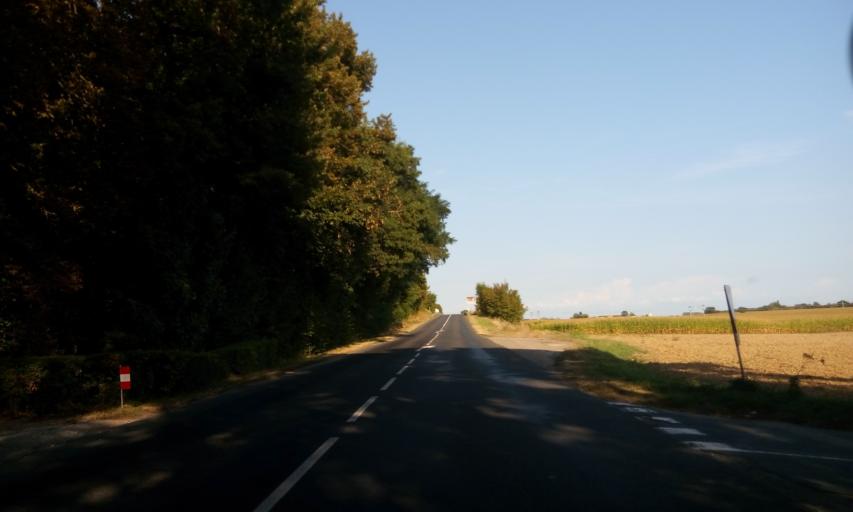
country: FR
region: Rhone-Alpes
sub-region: Departement de l'Ain
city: Villeneuve
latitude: 46.0006
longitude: 4.8550
